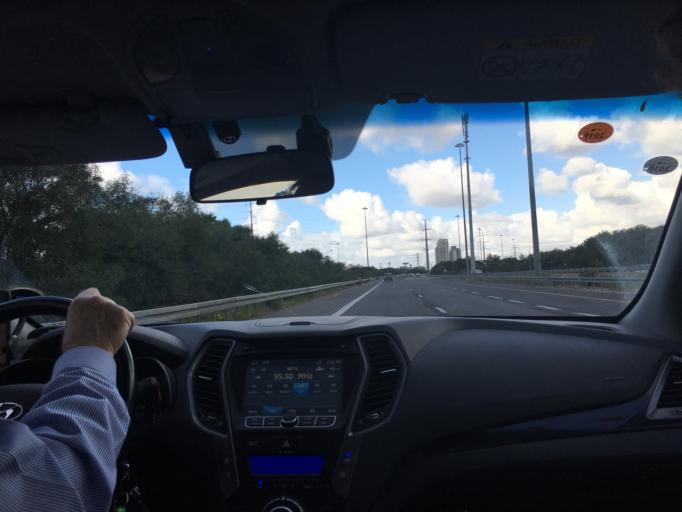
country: IL
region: Central District
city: Rishon LeZiyyon
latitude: 31.9598
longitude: 34.7857
